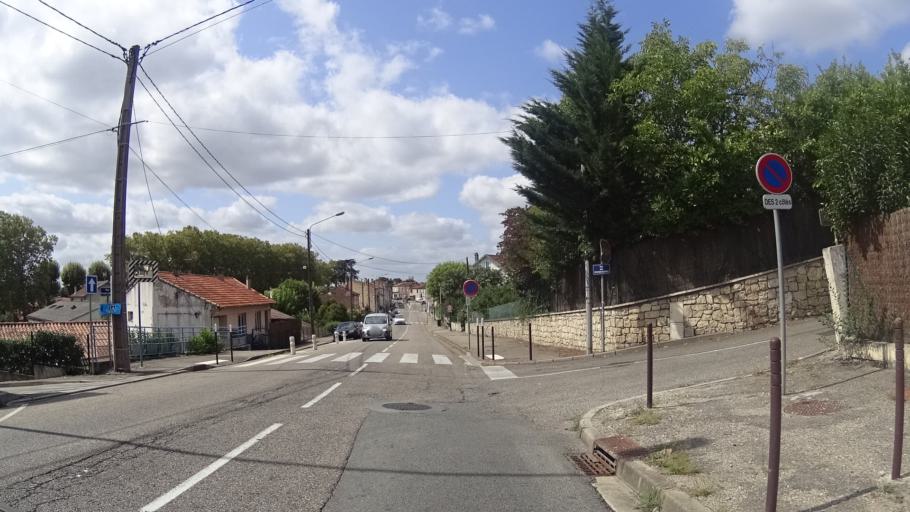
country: FR
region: Aquitaine
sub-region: Departement du Lot-et-Garonne
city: Agen
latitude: 44.2112
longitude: 0.6325
